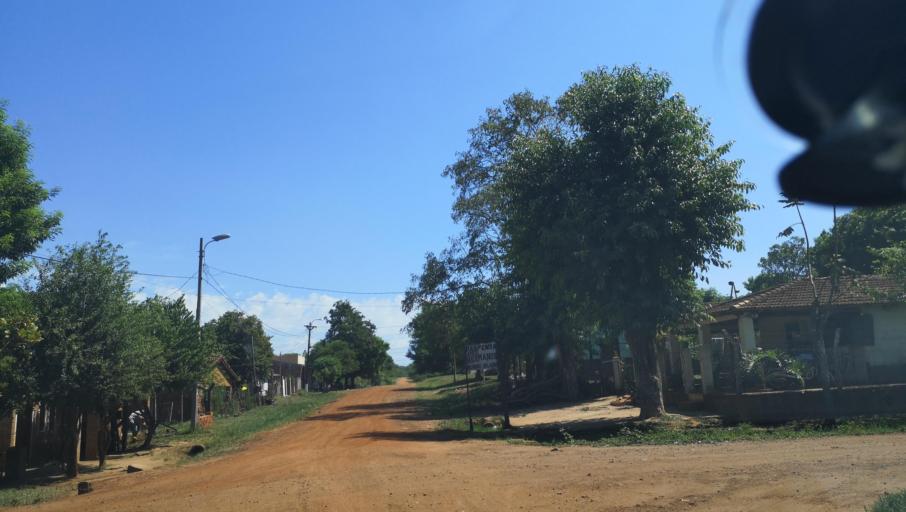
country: PY
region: Itapua
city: Carmen del Parana
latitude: -27.1684
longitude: -56.2476
